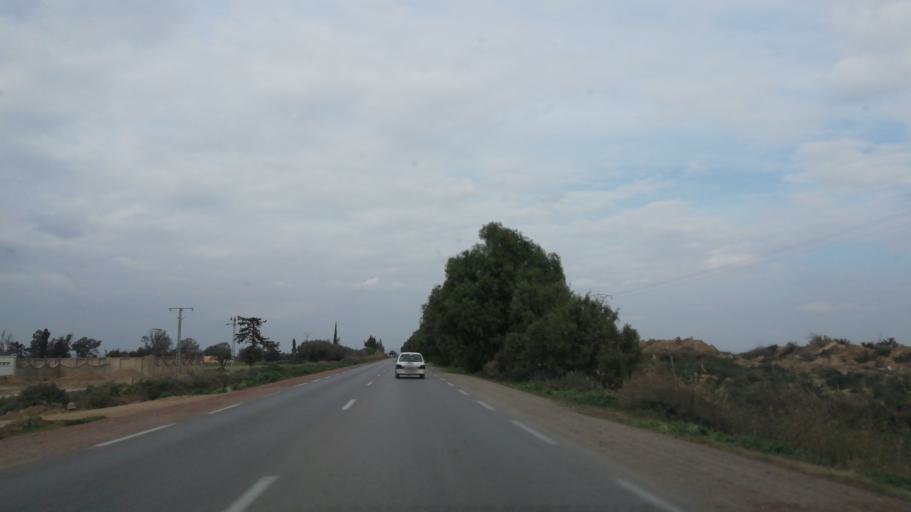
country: DZ
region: Mostaganem
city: Mostaganem
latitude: 35.6587
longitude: 0.0588
